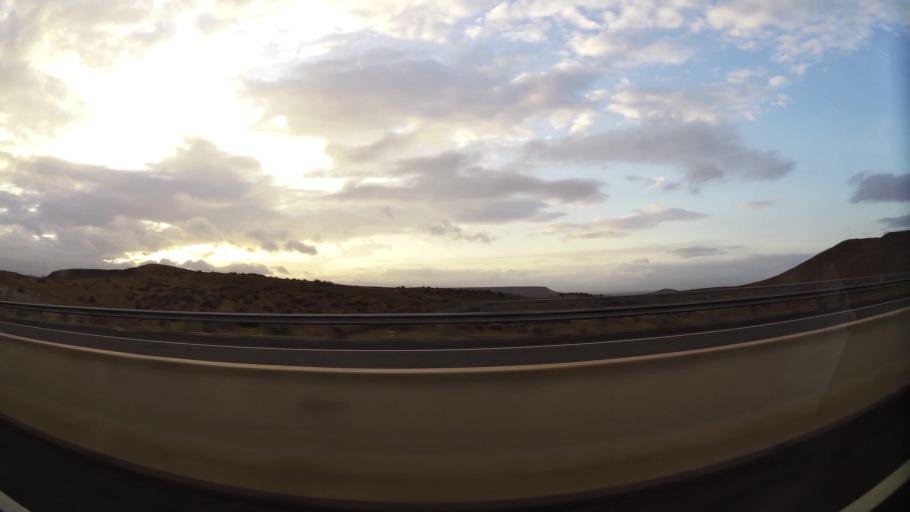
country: MA
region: Oriental
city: Taourirt
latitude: 34.4679
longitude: -3.0367
